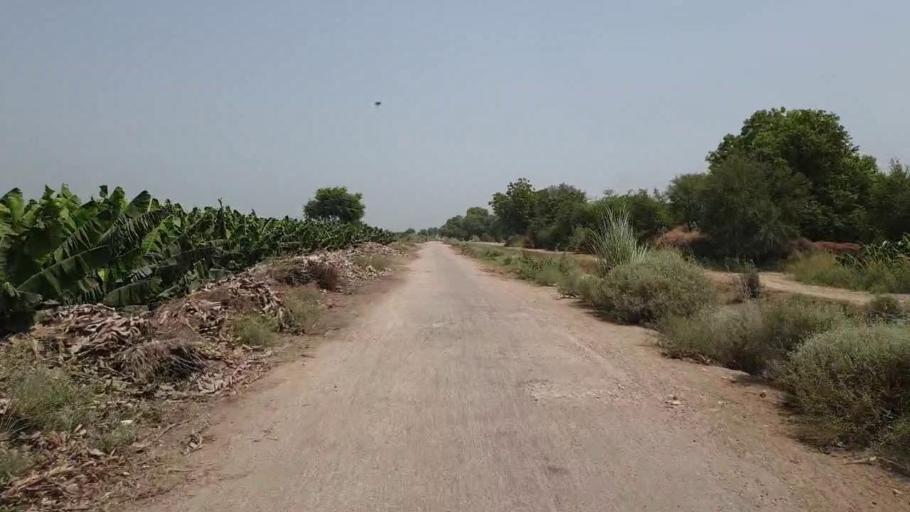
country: PK
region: Sindh
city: Nawabshah
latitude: 26.2859
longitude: 68.3102
